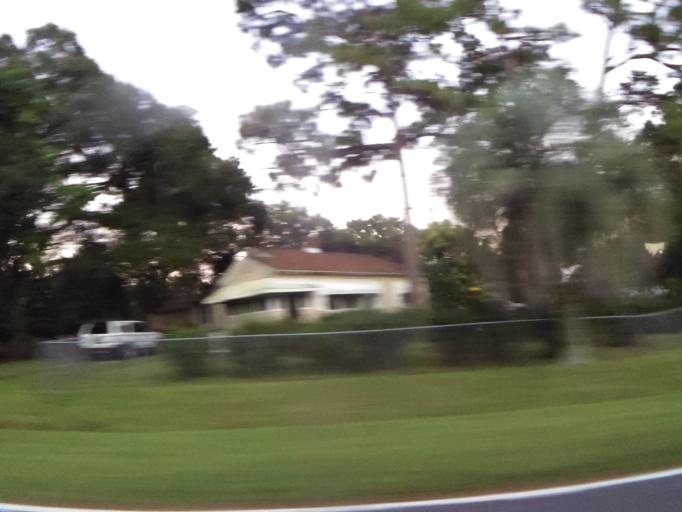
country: US
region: Florida
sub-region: Duval County
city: Jacksonville
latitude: 30.3011
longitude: -81.7220
